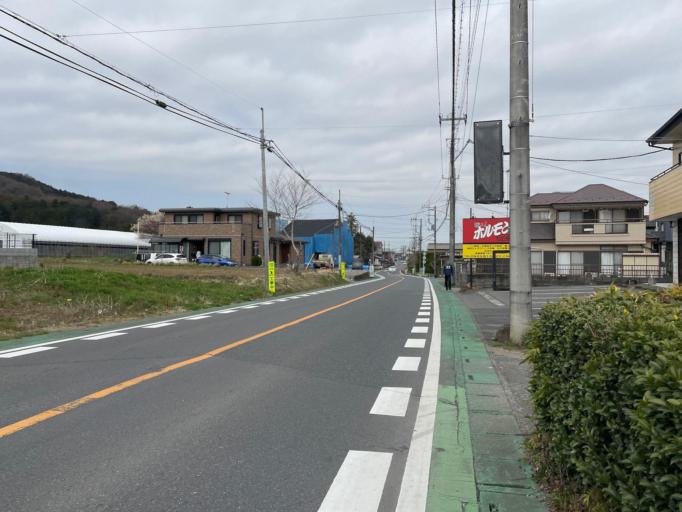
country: JP
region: Saitama
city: Ogawa
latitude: 36.0530
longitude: 139.3166
